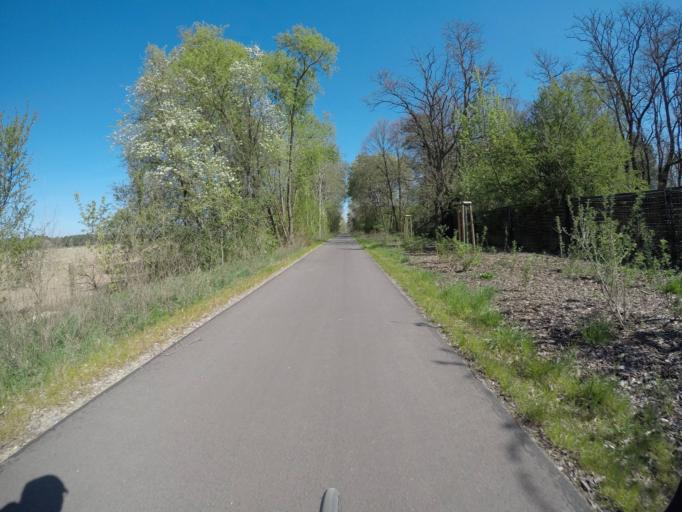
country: DE
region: Brandenburg
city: Werftpfuhl
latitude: 52.6389
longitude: 13.7694
